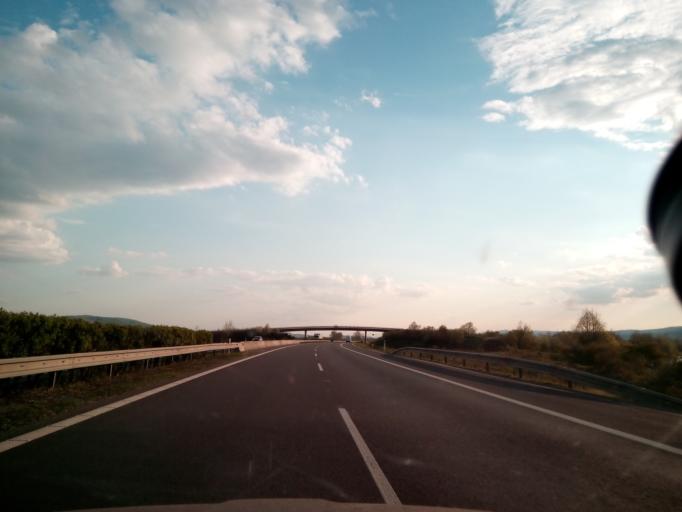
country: SK
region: Nitriansky
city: Ilava
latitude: 49.0185
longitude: 18.2557
